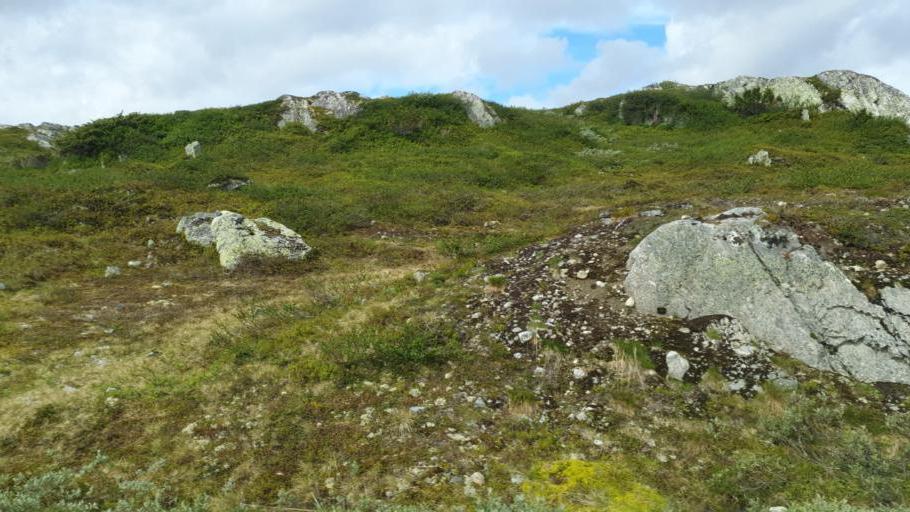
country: NO
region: Oppland
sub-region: Vestre Slidre
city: Slidre
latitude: 61.3251
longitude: 8.8046
